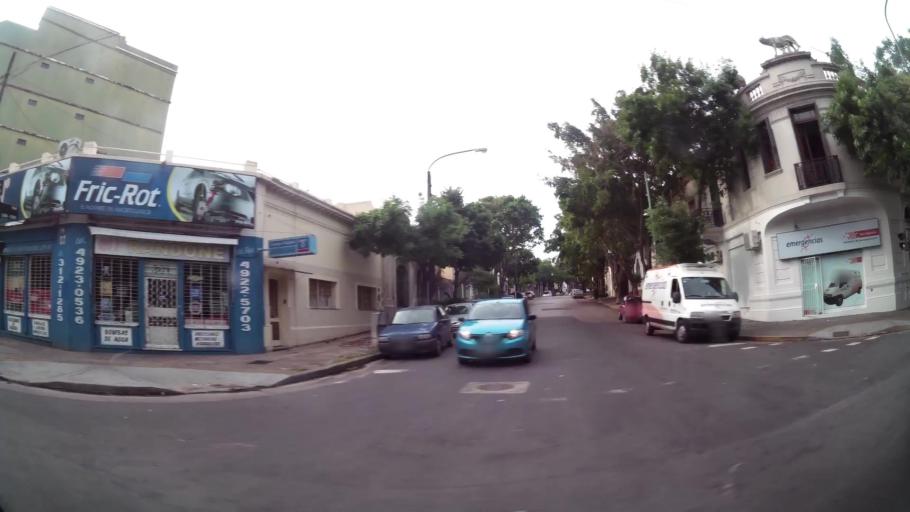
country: AR
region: Buenos Aires F.D.
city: Villa Santa Rita
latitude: -34.6320
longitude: -58.4298
